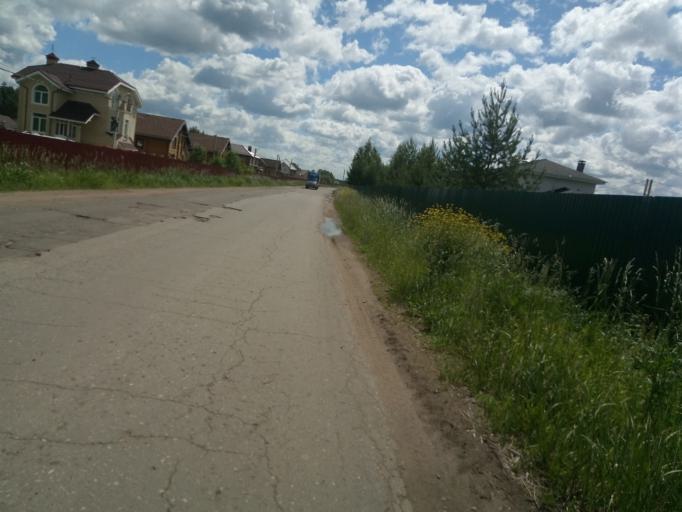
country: RU
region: Jaroslavl
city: Yaroslavl
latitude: 57.6537
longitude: 39.9878
